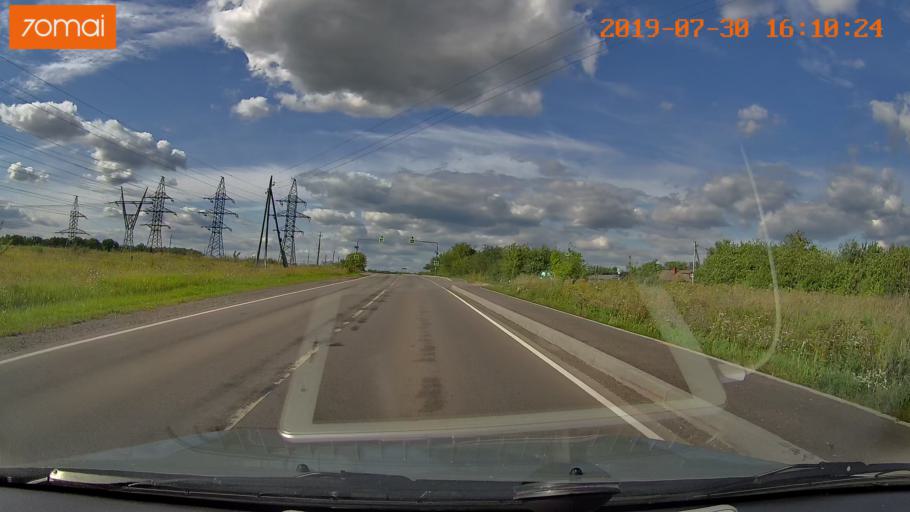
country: RU
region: Moskovskaya
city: Peski
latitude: 55.2622
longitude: 38.7156
